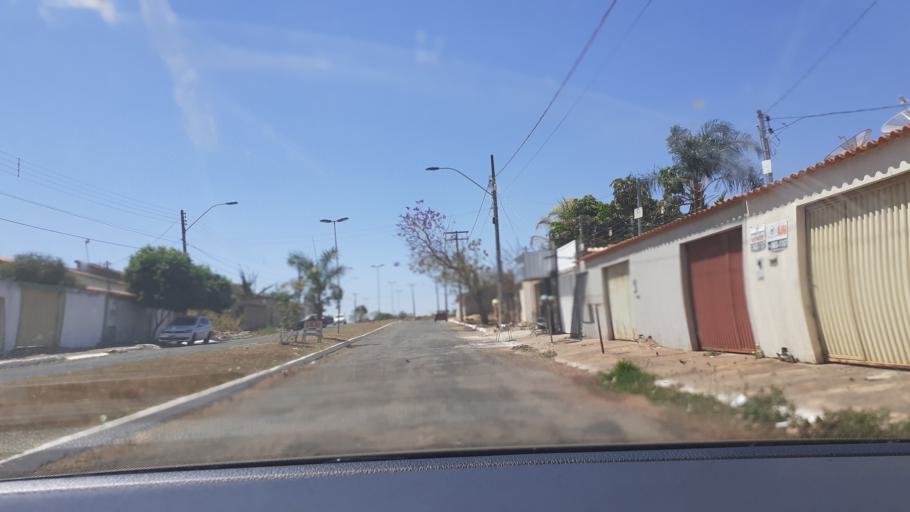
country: BR
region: Goias
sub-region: Caldas Novas
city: Caldas Novas
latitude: -17.7414
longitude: -48.6438
